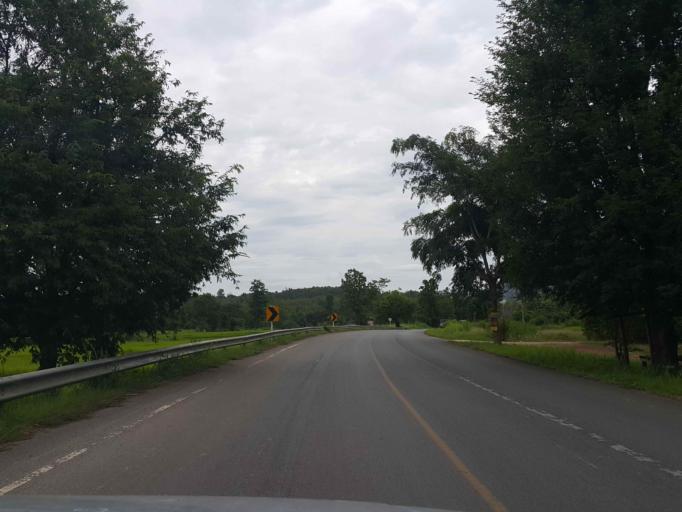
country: TH
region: Lampang
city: Thoen
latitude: 17.5427
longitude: 99.3381
